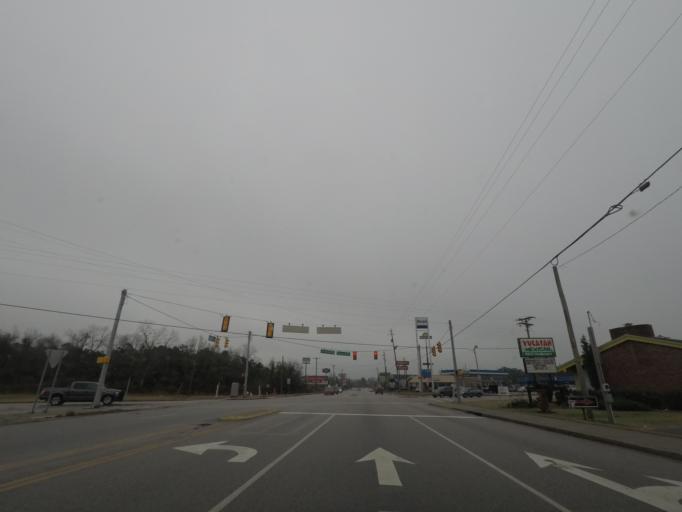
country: US
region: South Carolina
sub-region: Clarendon County
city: Manning
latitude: 33.7031
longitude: -80.2415
